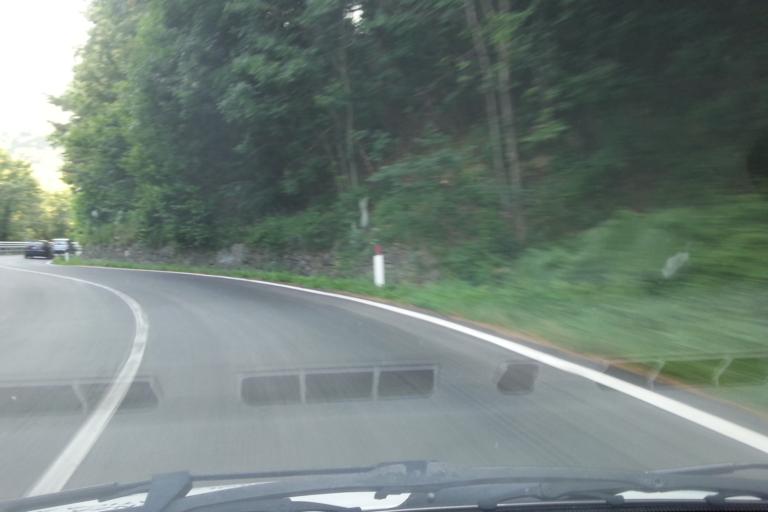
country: IT
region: Piedmont
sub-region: Provincia di Torino
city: Venaus
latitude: 45.1591
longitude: 6.9965
